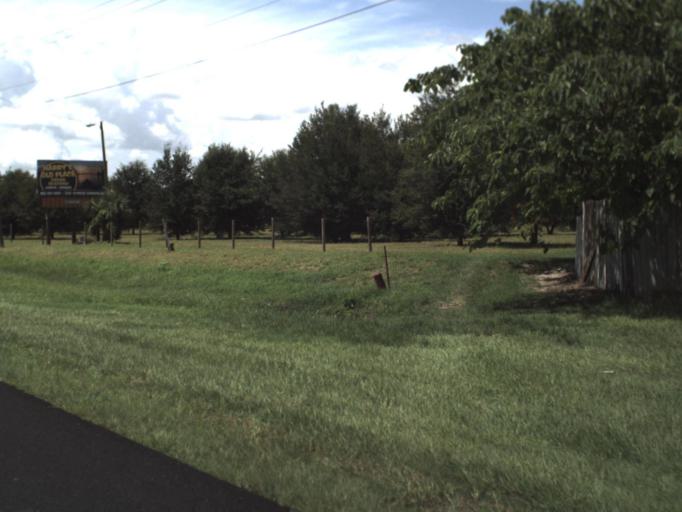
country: US
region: Florida
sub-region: Polk County
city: Cypress Gardens
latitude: 27.9786
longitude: -81.6544
